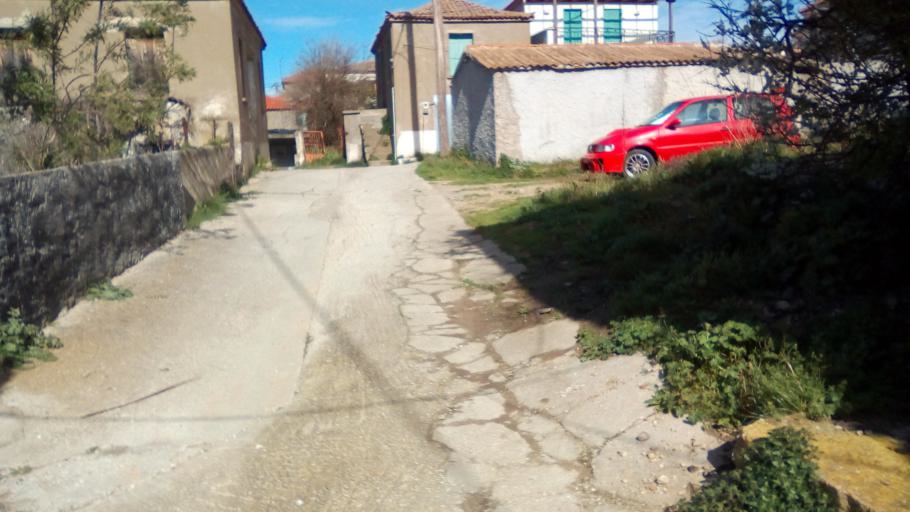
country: GR
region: North Aegean
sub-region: Nomos Lesvou
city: Myrina
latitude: 39.9333
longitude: 25.2318
